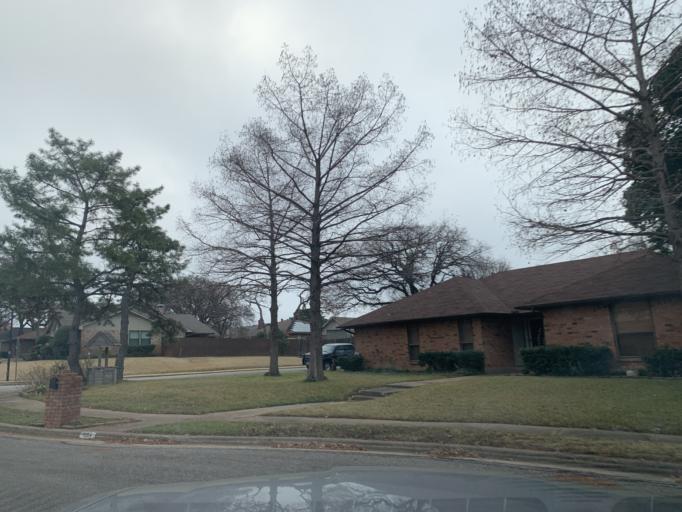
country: US
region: Texas
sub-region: Tarrant County
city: Bedford
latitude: 32.8361
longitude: -97.1501
